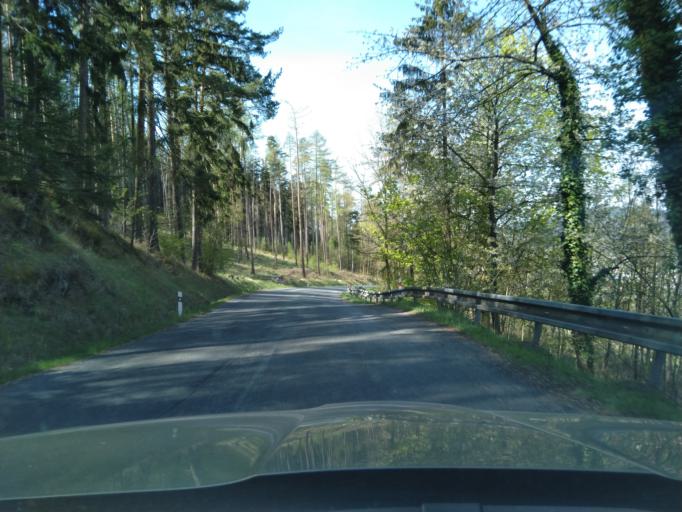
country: CZ
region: Plzensky
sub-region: Okres Klatovy
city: Susice
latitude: 49.2435
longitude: 13.5508
